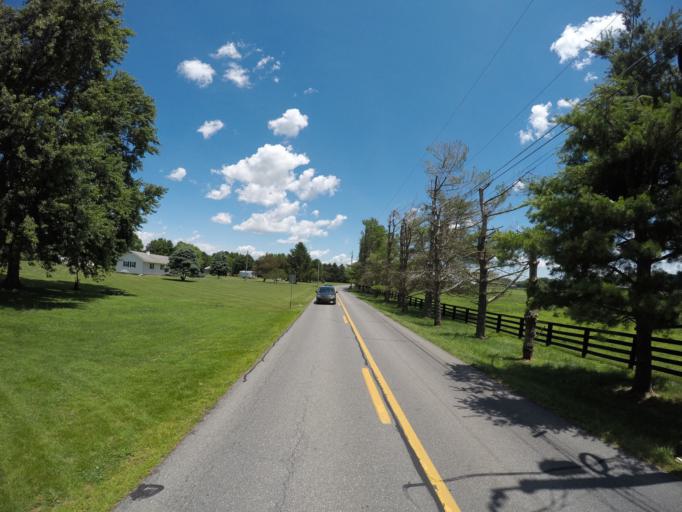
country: US
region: Delaware
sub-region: New Castle County
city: Middletown
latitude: 39.4812
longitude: -75.7498
